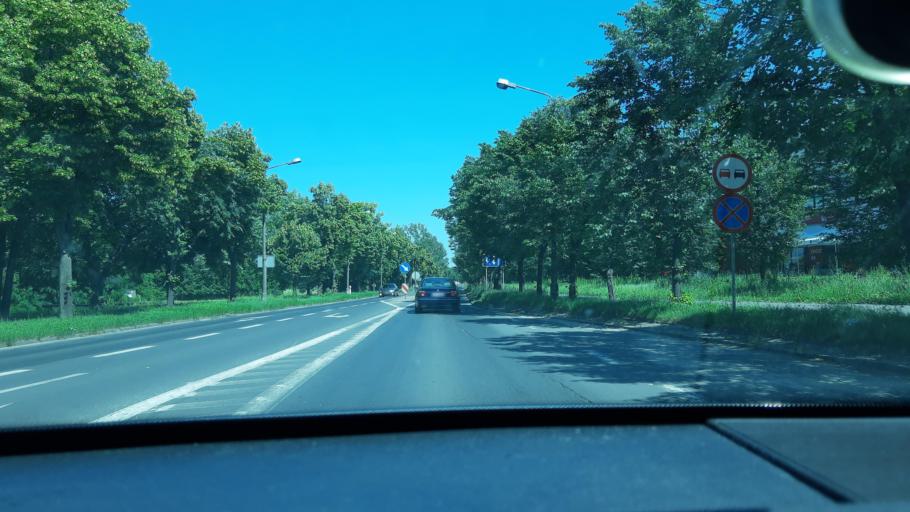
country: PL
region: Lodz Voivodeship
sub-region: Powiat zdunskowolski
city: Zdunska Wola
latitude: 51.6075
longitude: 18.9308
